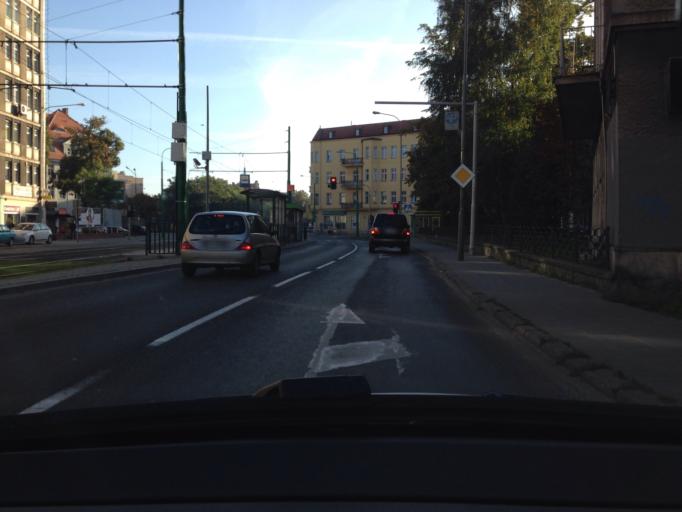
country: PL
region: Greater Poland Voivodeship
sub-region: Poznan
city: Poznan
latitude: 52.4050
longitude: 16.8988
